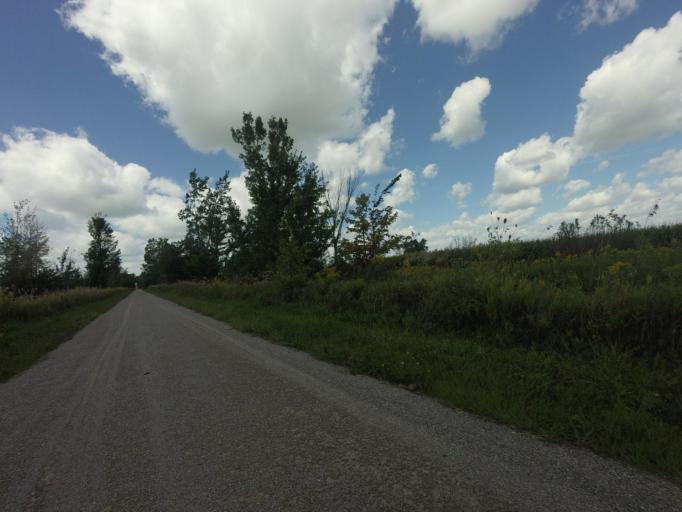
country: CA
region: Ontario
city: North Perth
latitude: 43.5781
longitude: -81.0526
